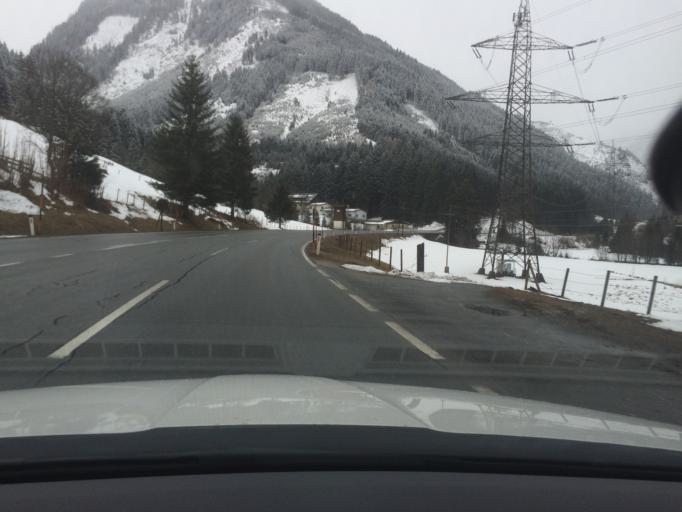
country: AT
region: Salzburg
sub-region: Politischer Bezirk Zell am See
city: Mittersill
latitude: 47.2282
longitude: 12.4929
